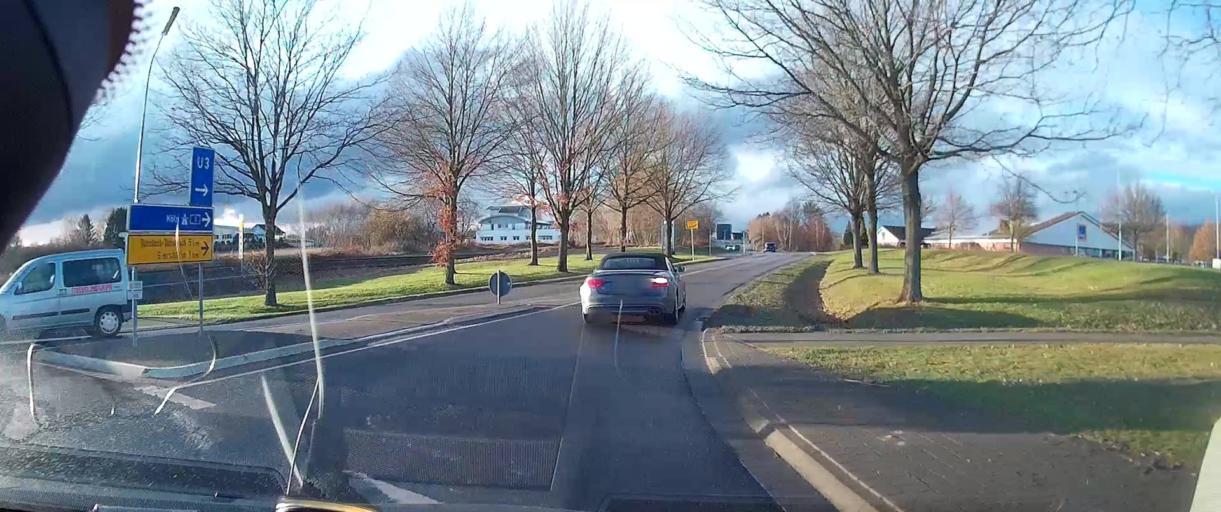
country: DE
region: Rheinland-Pfalz
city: Wirges
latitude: 50.4762
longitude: 7.7878
